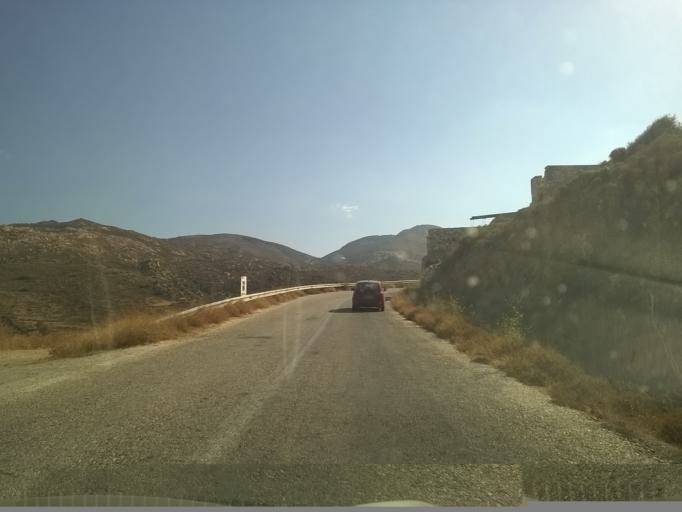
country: GR
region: South Aegean
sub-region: Nomos Kykladon
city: Naxos
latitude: 37.0963
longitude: 25.4432
